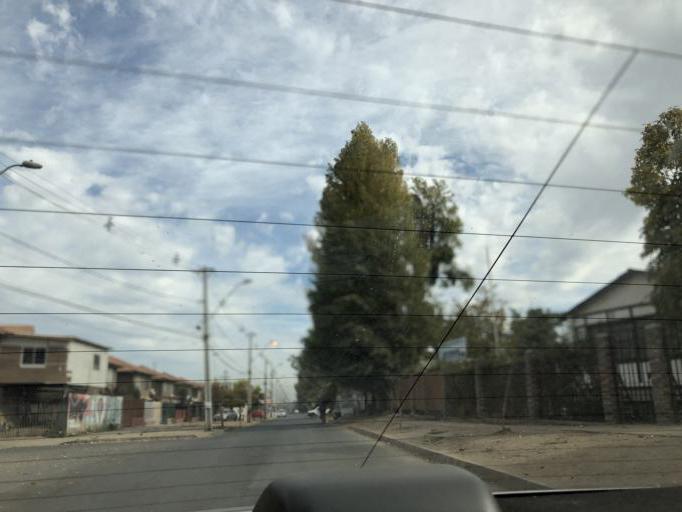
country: CL
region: Santiago Metropolitan
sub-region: Provincia de Cordillera
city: Puente Alto
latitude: -33.6100
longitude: -70.5230
